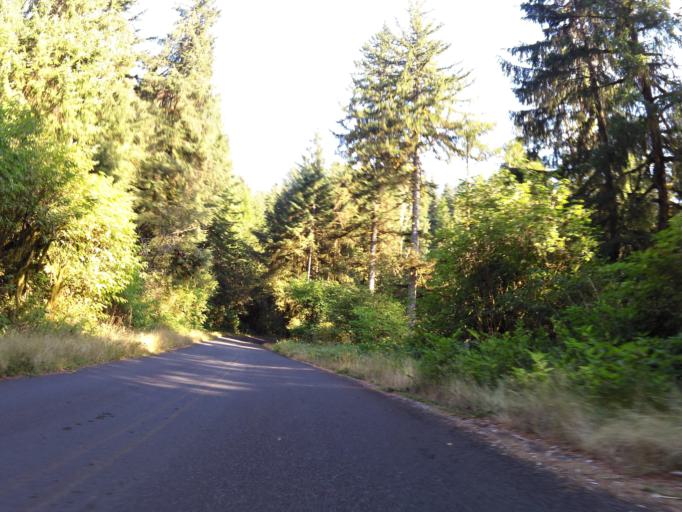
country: US
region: Oregon
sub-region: Lincoln County
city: Rose Lodge
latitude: 45.0398
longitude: -123.9123
